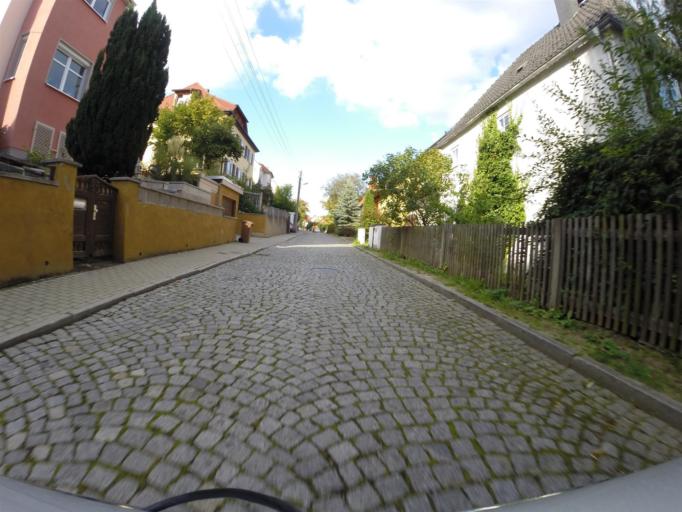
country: DE
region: Thuringia
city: Jena
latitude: 50.9446
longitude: 11.5928
